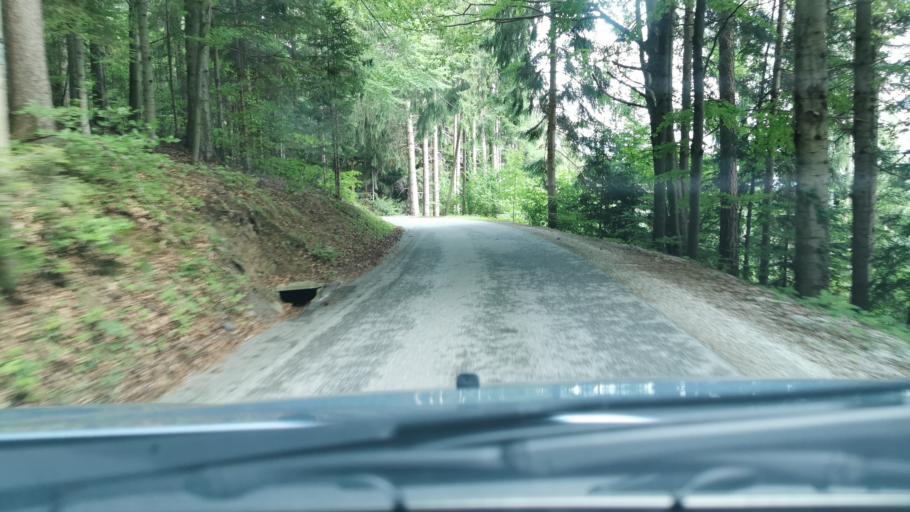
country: AT
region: Styria
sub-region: Politischer Bezirk Weiz
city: Koglhof
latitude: 47.3220
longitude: 15.6668
